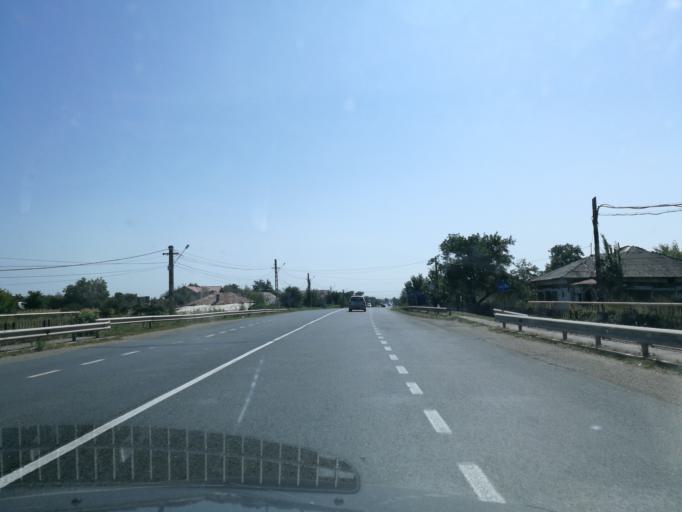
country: RO
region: Bacau
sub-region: Comuna Racaciuni
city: Racaciuni
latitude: 46.3289
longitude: 27.0094
